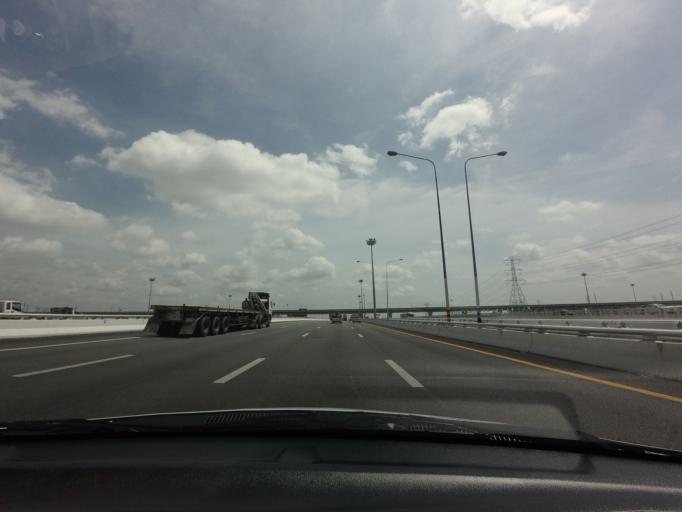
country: TH
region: Bangkok
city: Saphan Sung
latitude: 13.7338
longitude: 100.7028
